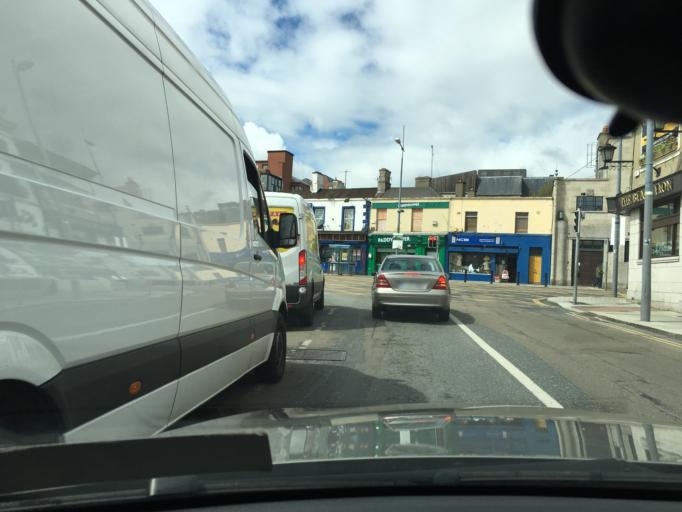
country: IE
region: Leinster
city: Crumlin
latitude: 53.3394
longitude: -6.3205
